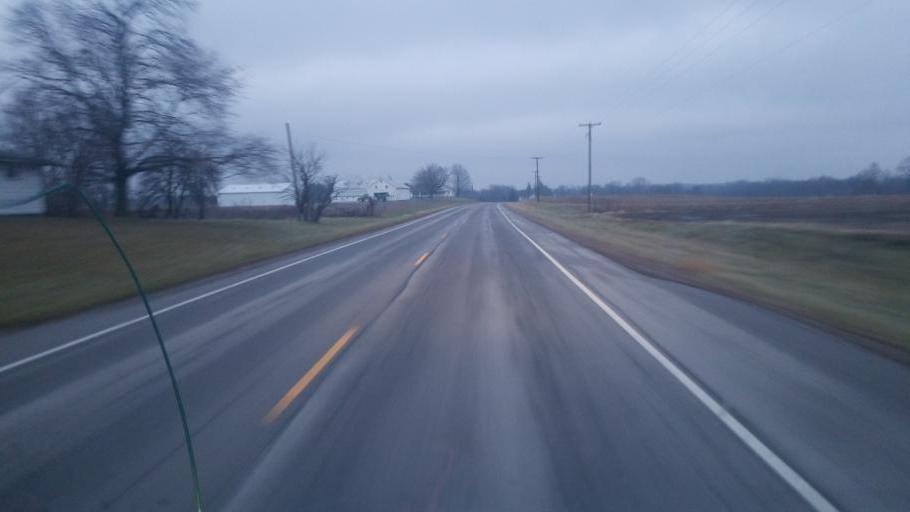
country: US
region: Ohio
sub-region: Crawford County
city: Bucyrus
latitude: 40.8438
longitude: -83.1085
